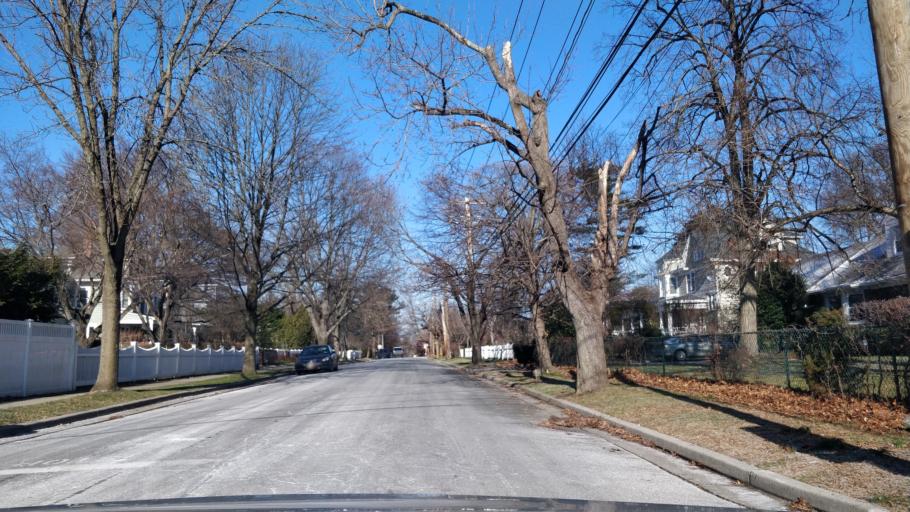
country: US
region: New York
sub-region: Nassau County
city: Sea Cliff
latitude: 40.8439
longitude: -73.6397
